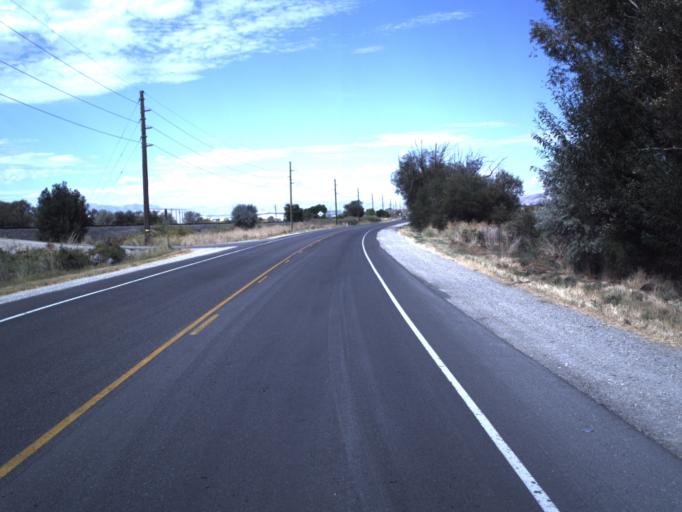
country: US
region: Utah
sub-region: Box Elder County
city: Brigham City
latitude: 41.5297
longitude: -112.0368
